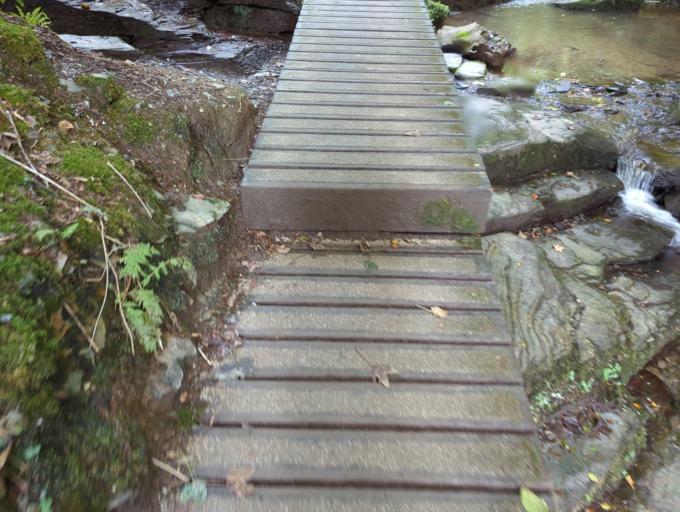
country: GB
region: England
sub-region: Cornwall
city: Tintagel
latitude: 50.6650
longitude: -4.7188
